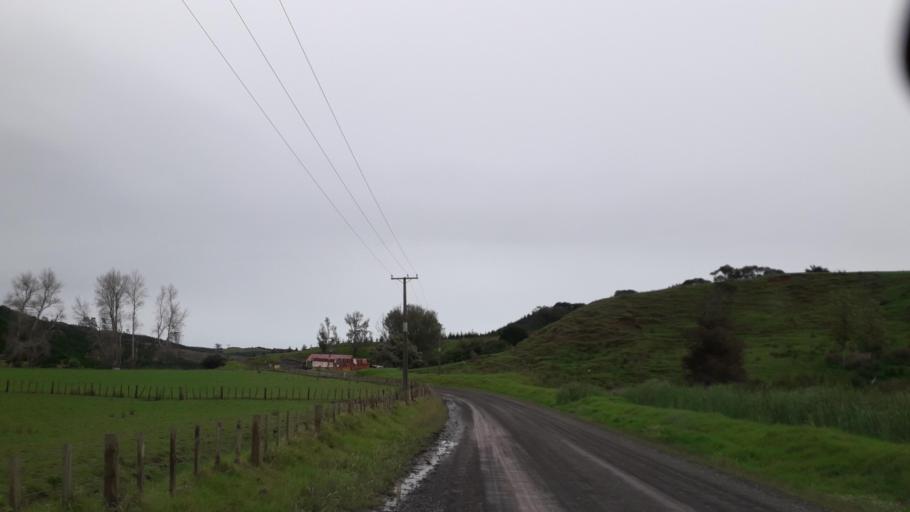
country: NZ
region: Northland
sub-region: Far North District
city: Ahipara
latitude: -35.4236
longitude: 173.3588
